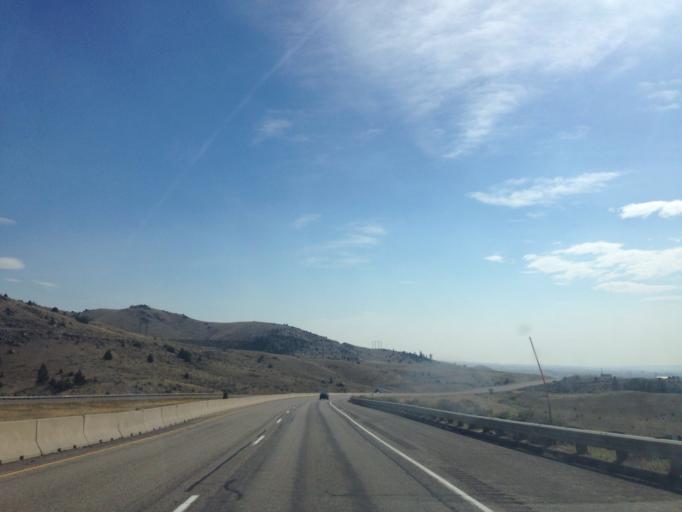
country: US
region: Montana
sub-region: Jefferson County
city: Whitehall
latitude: 45.9137
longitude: -112.2756
